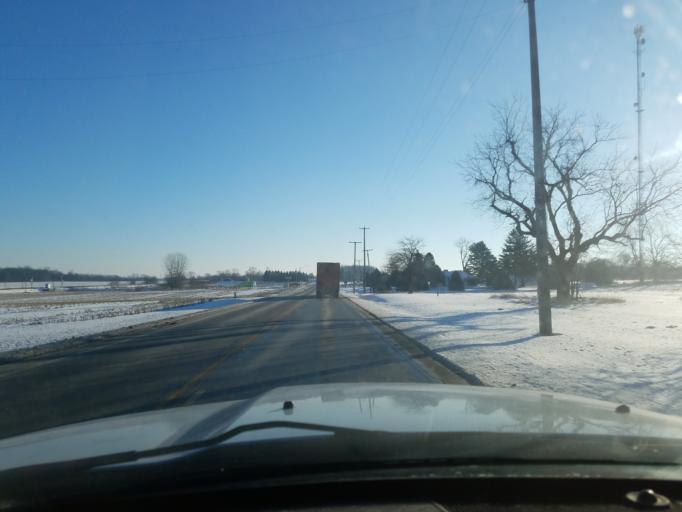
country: US
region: Indiana
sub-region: Noble County
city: Albion
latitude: 41.4531
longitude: -85.4272
